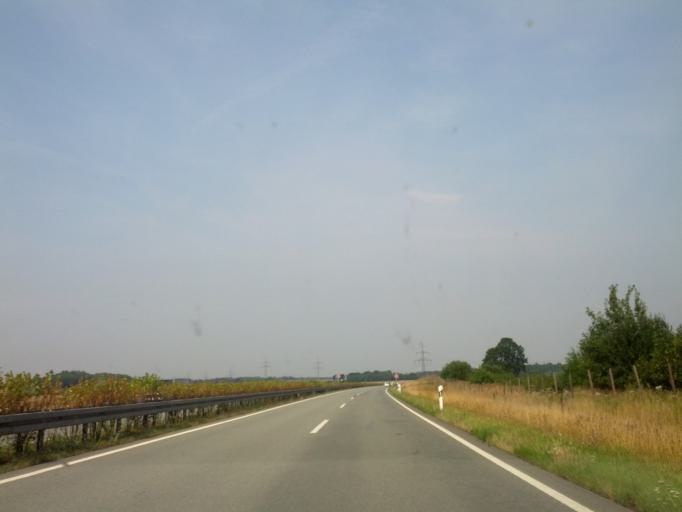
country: DE
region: Mecklenburg-Vorpommern
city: Brandshagen
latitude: 54.1930
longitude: 13.1602
